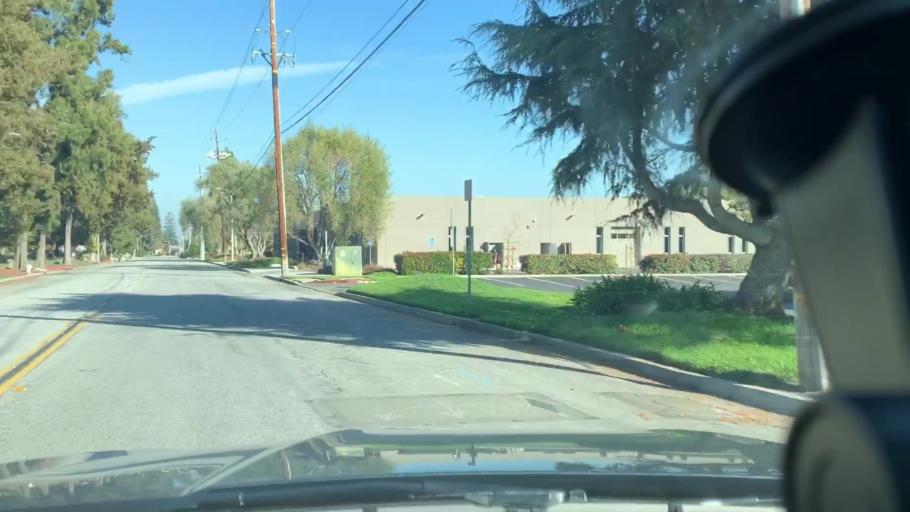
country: US
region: California
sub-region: Santa Clara County
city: Sunnyvale
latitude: 37.3868
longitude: -122.0346
